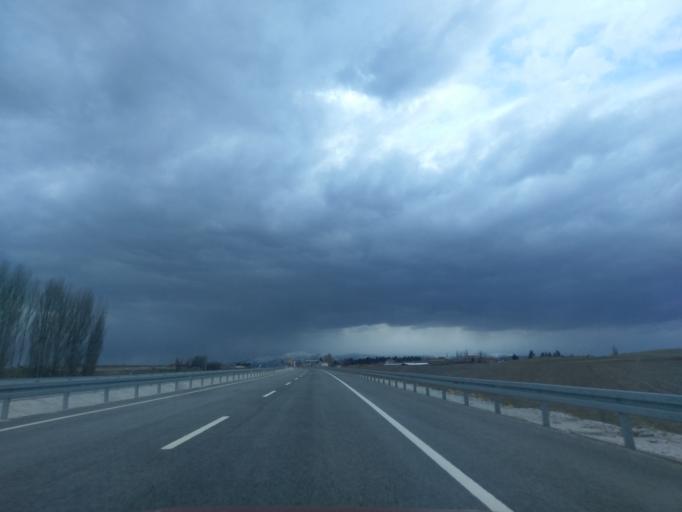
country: TR
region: Kuetahya
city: Cavdarhisar
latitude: 39.2205
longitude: 29.6776
